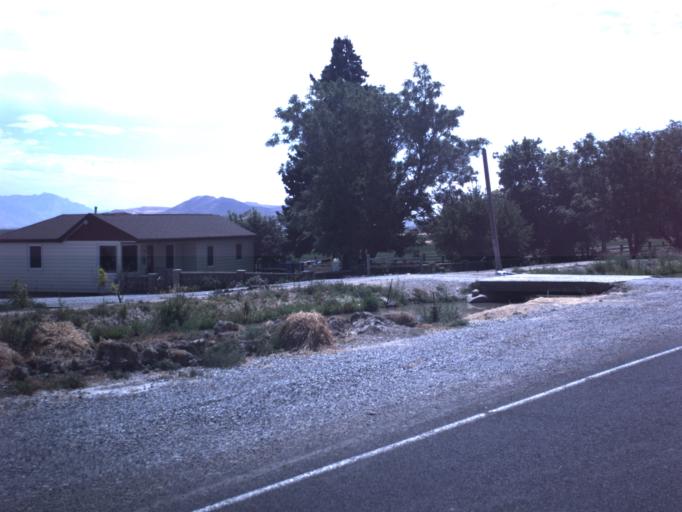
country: US
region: Utah
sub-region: Box Elder County
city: Tremonton
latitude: 41.6909
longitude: -112.2959
